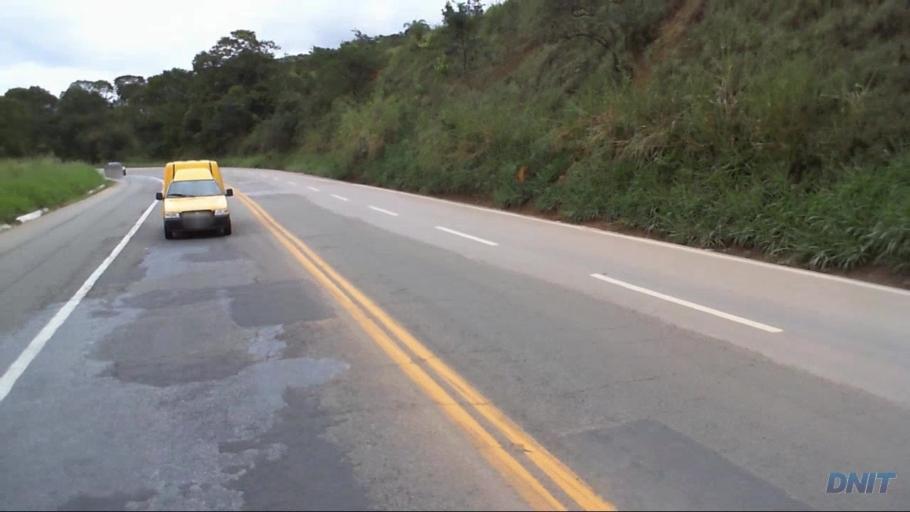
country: BR
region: Minas Gerais
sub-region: Barao De Cocais
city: Barao de Cocais
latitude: -19.7966
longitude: -43.4254
